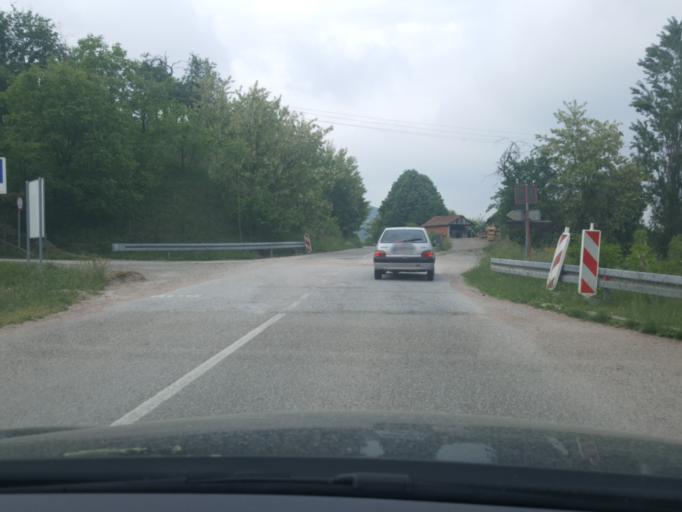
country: RS
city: Kamenica
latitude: 44.2163
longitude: 19.7158
